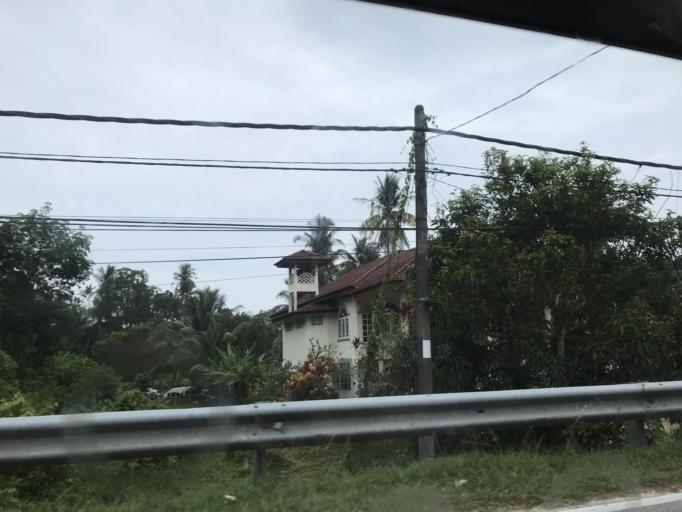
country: MY
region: Kelantan
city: Kota Bharu
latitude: 6.1642
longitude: 102.2265
